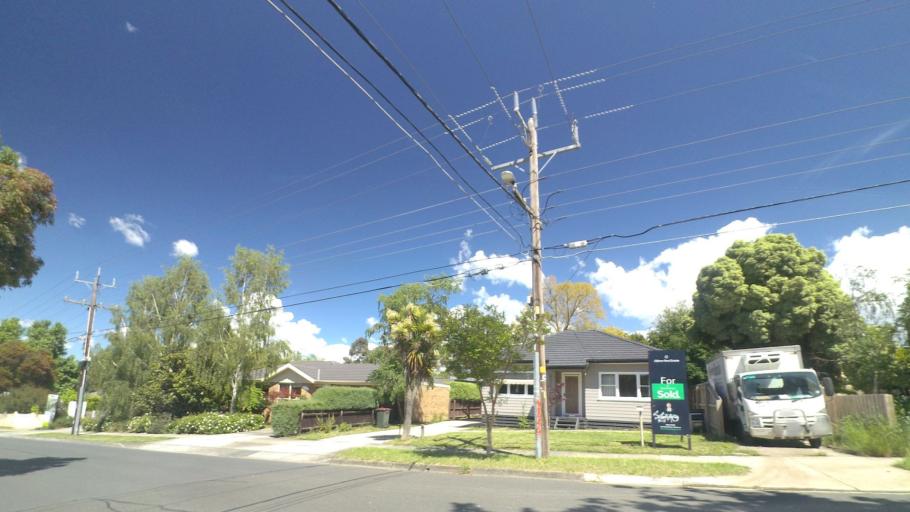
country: AU
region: Victoria
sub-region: Maroondah
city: Croydon South
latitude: -37.8203
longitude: 145.2752
